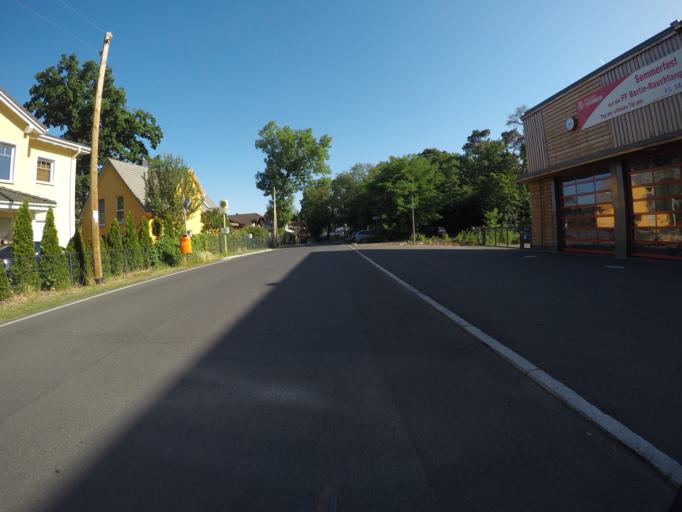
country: DE
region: Berlin
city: Schmockwitz
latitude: 52.3471
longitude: 13.6456
